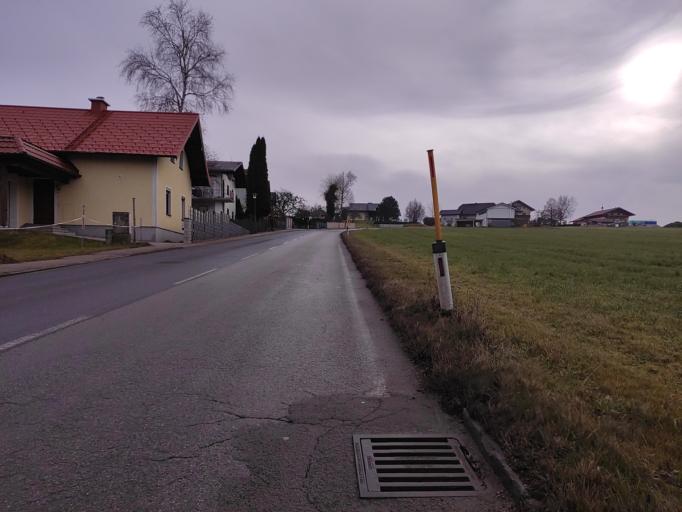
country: AT
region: Salzburg
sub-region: Politischer Bezirk Salzburg-Umgebung
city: Berndorf bei Salzburg
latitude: 47.9943
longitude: 13.0638
